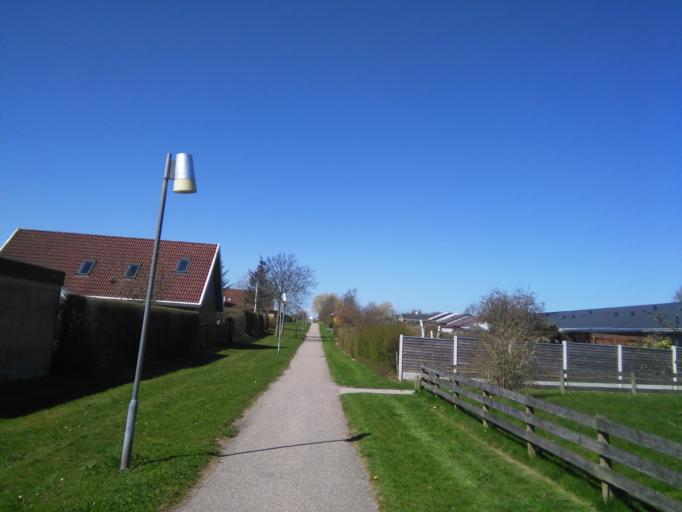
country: DK
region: Central Jutland
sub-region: Arhus Kommune
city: Marslet
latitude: 56.0888
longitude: 10.1531
